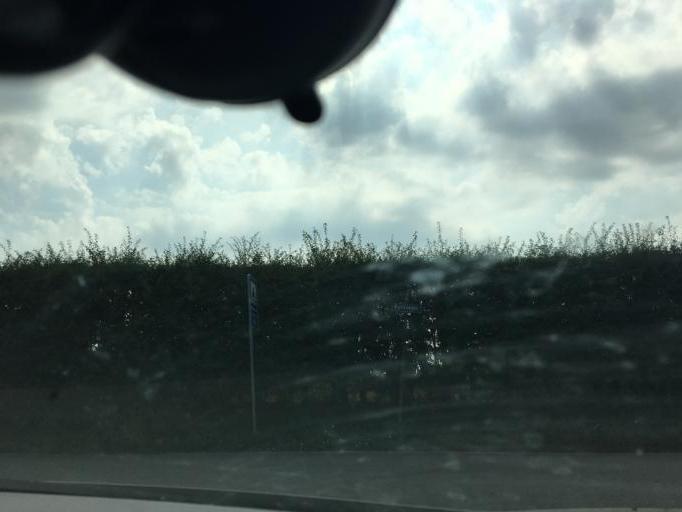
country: DK
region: South Denmark
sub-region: Middelfart Kommune
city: Norre Aby
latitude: 55.5064
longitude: 9.8841
